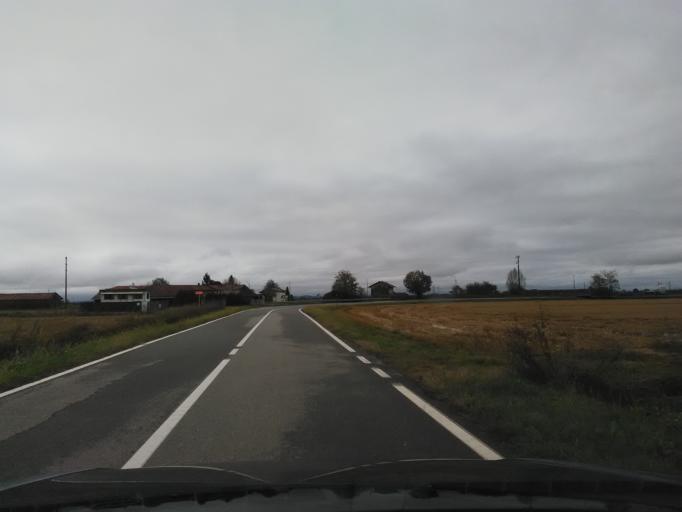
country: IT
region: Piedmont
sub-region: Provincia di Vercelli
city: Olcenengo
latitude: 45.3470
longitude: 8.2982
